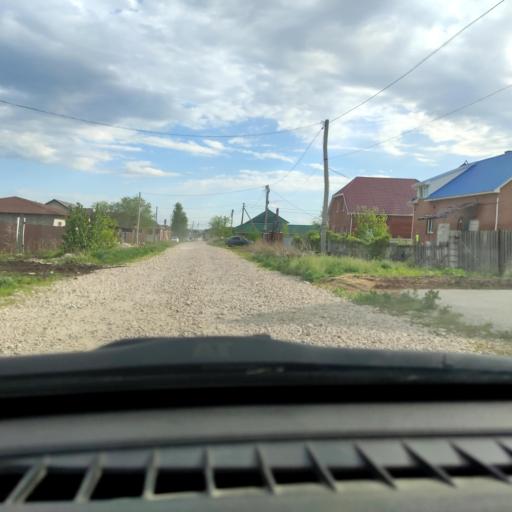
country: RU
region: Samara
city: Tol'yatti
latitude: 53.5681
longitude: 49.4083
